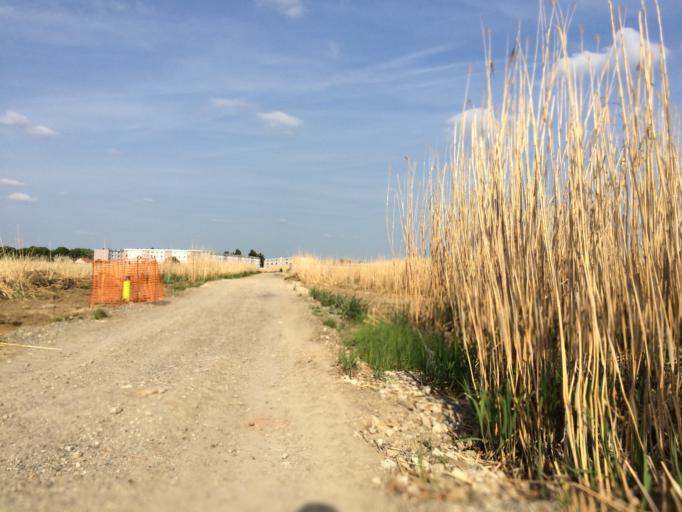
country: FR
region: Ile-de-France
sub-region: Departement de l'Essonne
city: Paray-Vieille-Poste
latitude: 48.7145
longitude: 2.3520
